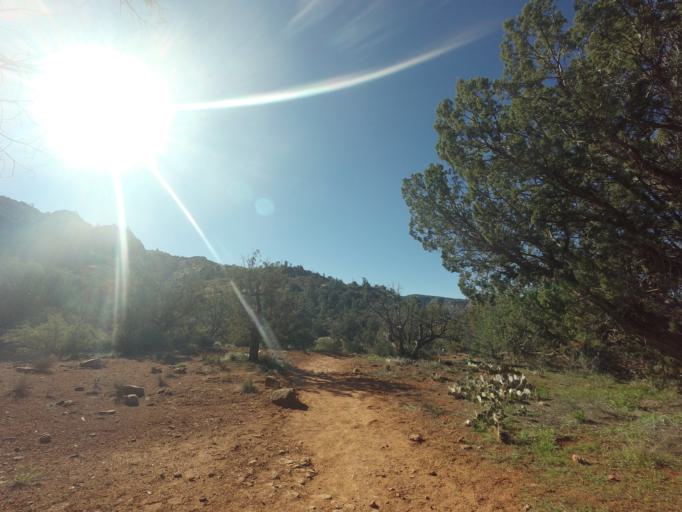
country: US
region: Arizona
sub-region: Yavapai County
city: West Sedona
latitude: 34.8207
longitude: -111.8078
